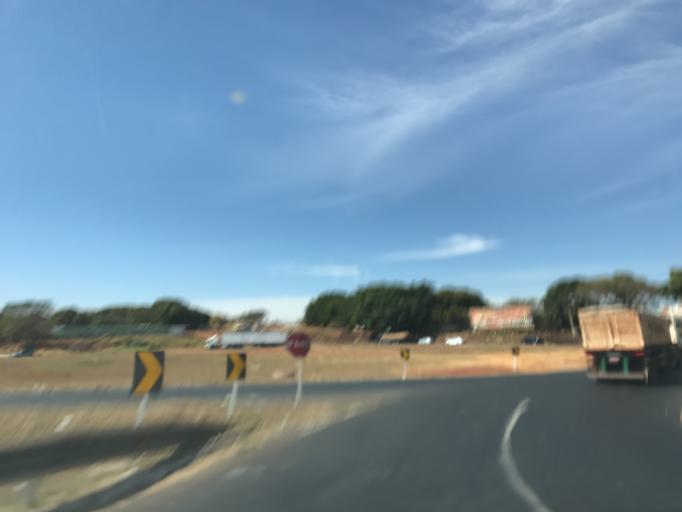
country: BR
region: Minas Gerais
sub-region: Monte Alegre De Minas
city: Monte Alegre de Minas
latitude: -18.8779
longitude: -49.0572
